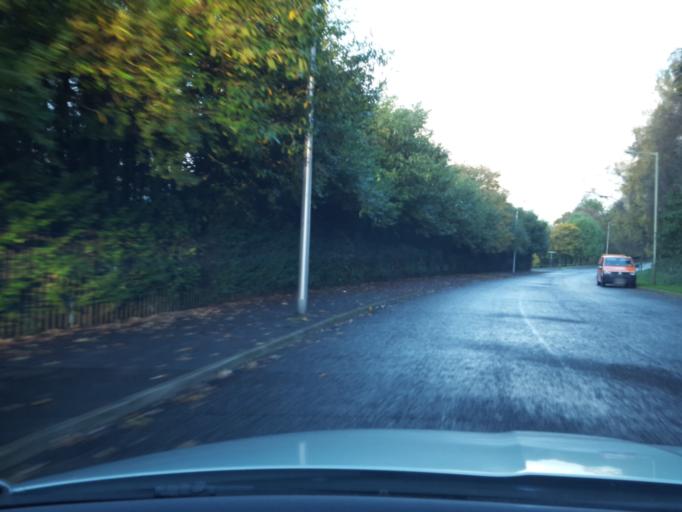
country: GB
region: Scotland
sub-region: Dundee City
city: Dundee
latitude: 56.4718
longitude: -2.9898
